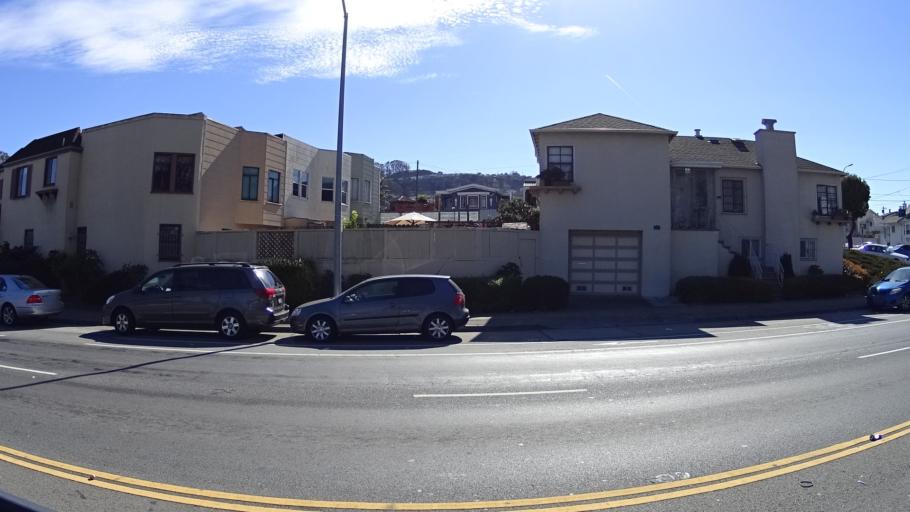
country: US
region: California
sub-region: San Mateo County
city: Daly City
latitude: 37.7129
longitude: -122.4324
